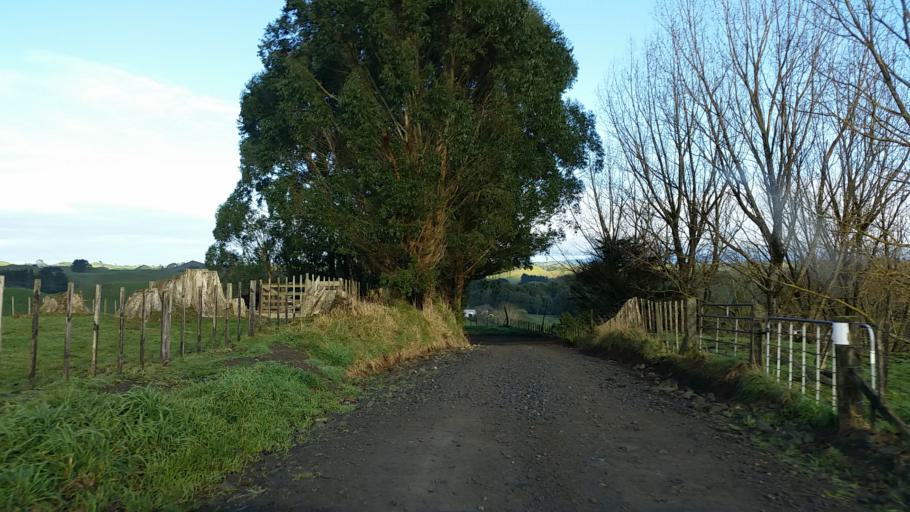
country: NZ
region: Taranaki
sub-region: South Taranaki District
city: Eltham
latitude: -39.2459
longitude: 174.3809
